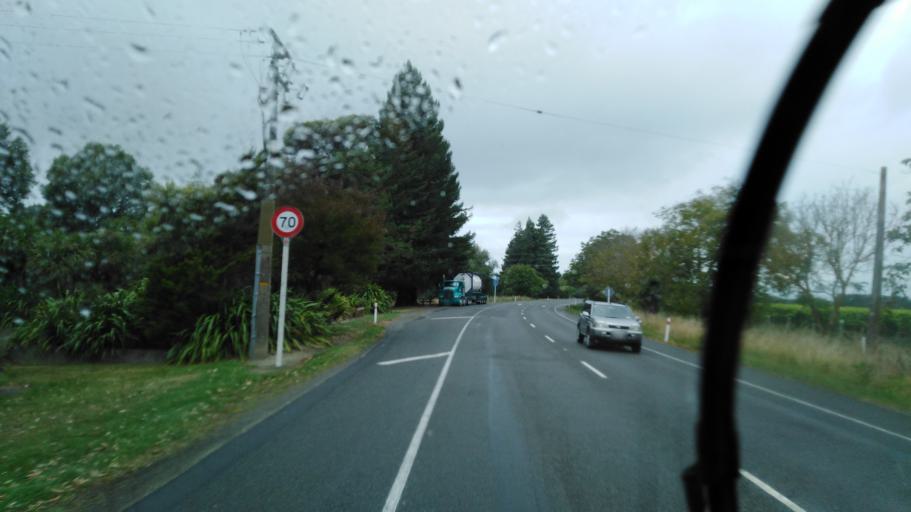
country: NZ
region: Marlborough
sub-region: Marlborough District
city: Blenheim
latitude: -41.4583
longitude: 173.9562
